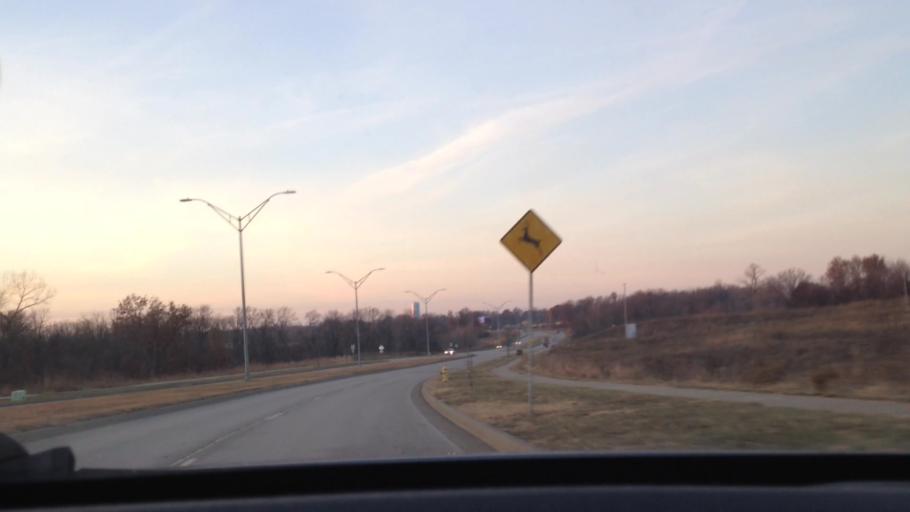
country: US
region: Missouri
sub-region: Clay County
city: Pleasant Valley
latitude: 39.2104
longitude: -94.4679
